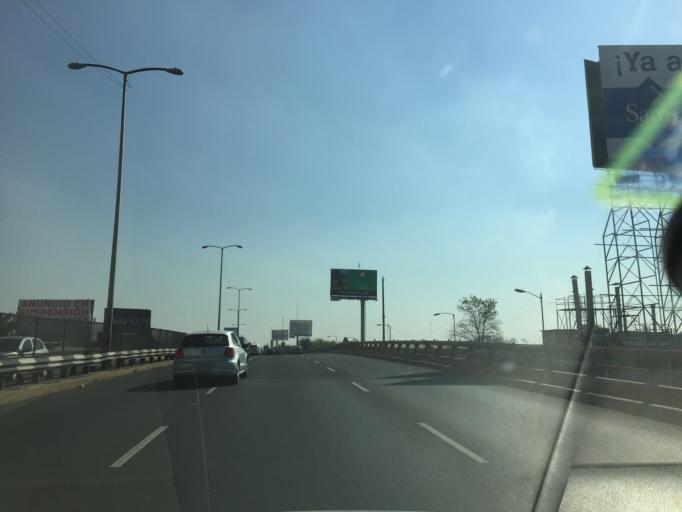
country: MX
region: Mexico City
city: Cuauhtemoc
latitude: 19.4634
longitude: -99.1544
